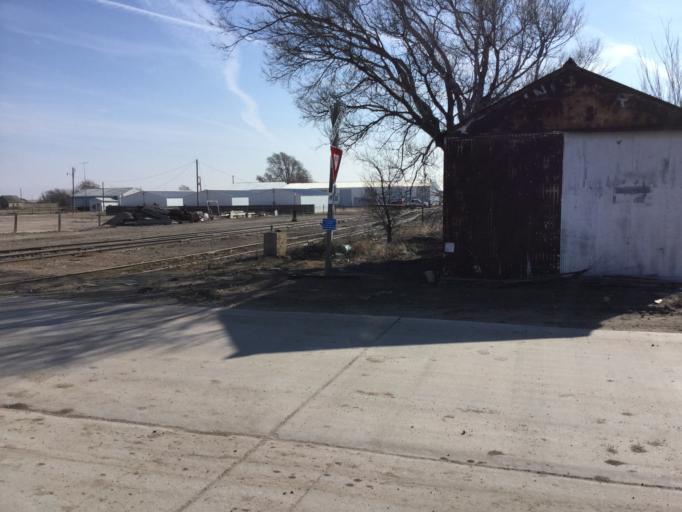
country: US
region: Kansas
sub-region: Scott County
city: Scott City
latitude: 38.4877
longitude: -100.9044
